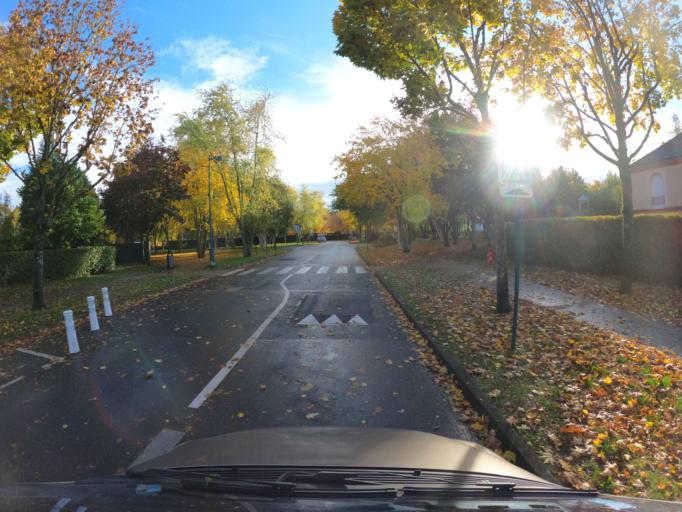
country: FR
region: Ile-de-France
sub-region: Departement de Seine-et-Marne
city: Bailly-Romainvilliers
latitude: 48.8436
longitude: 2.8229
